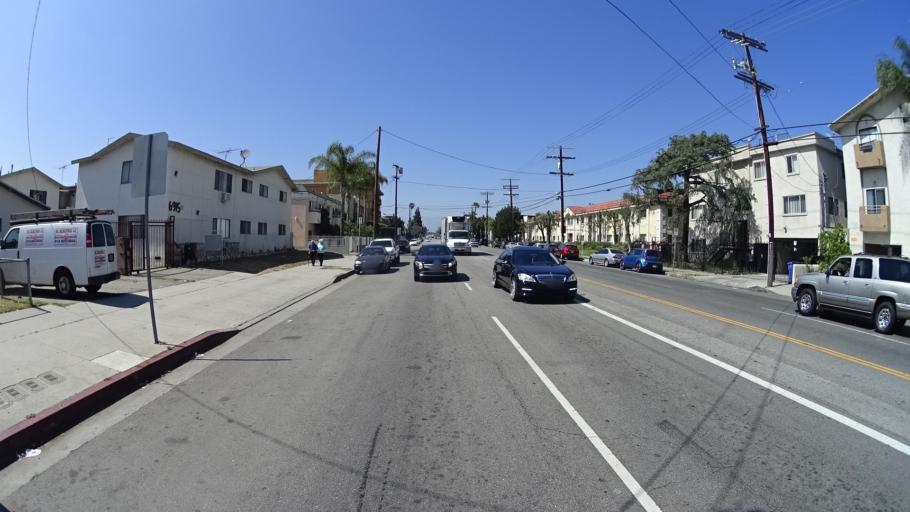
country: US
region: California
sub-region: Los Angeles County
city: Van Nuys
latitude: 34.1959
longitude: -118.4139
